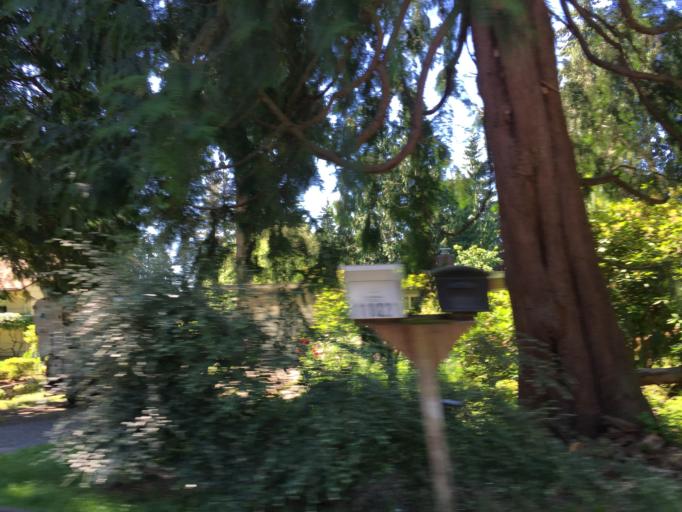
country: US
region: Washington
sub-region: King County
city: Bellevue
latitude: 47.6233
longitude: -122.1929
